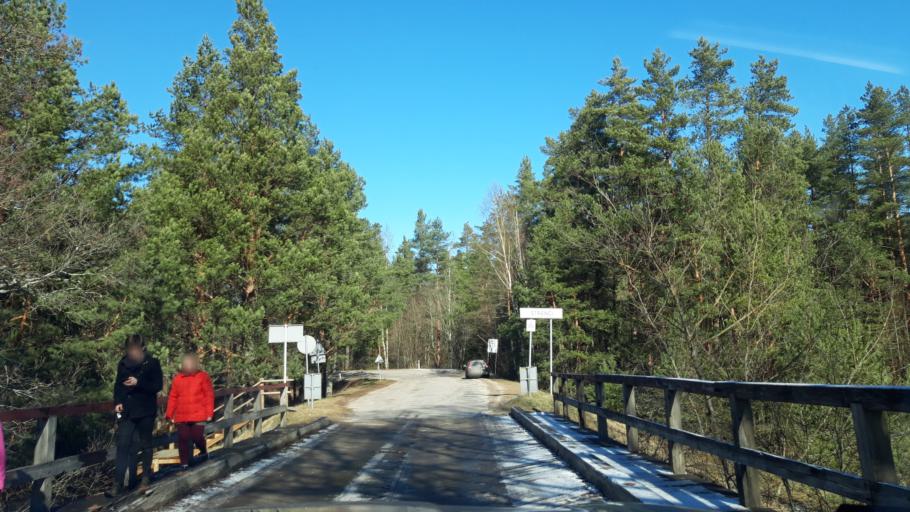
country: LV
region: Strenci
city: Strenci
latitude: 57.6190
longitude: 25.7015
